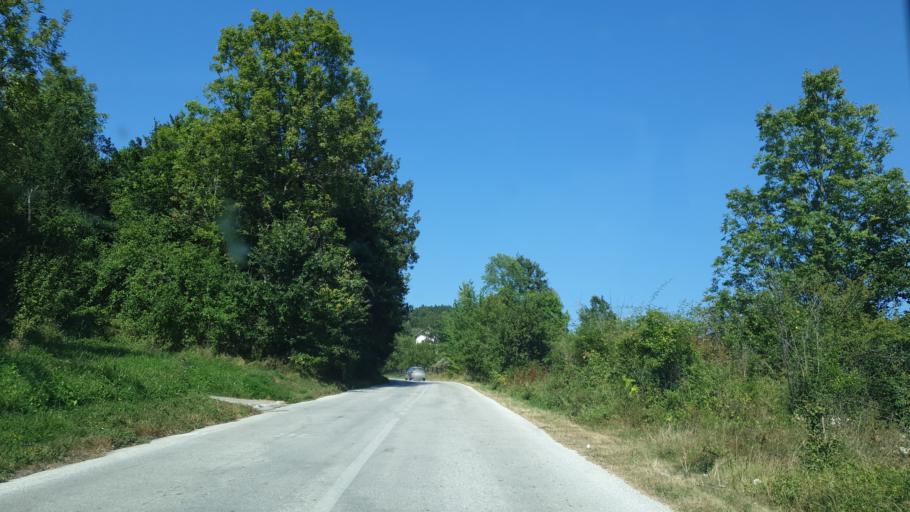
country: RS
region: Central Serbia
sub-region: Zlatiborski Okrug
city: Cajetina
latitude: 43.7150
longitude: 19.8297
